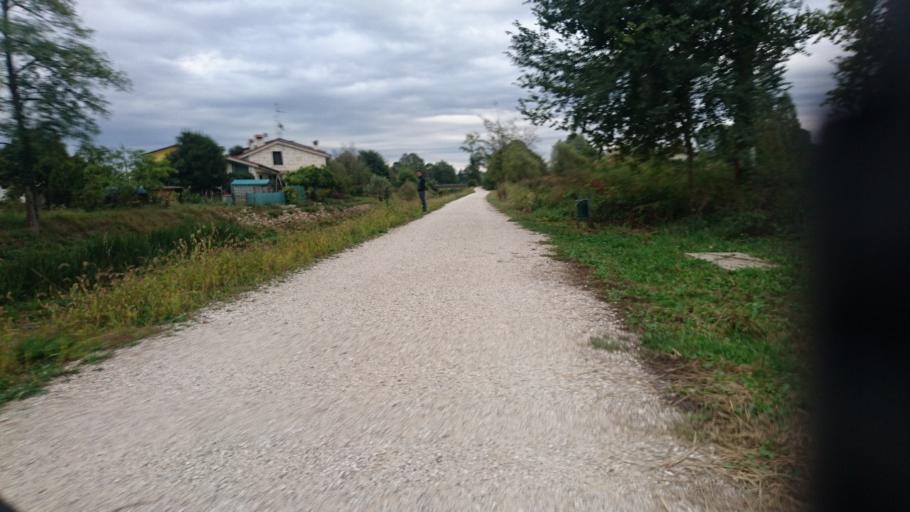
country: IT
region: Veneto
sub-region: Provincia di Vicenza
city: Creazzo
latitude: 45.5303
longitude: 11.4701
